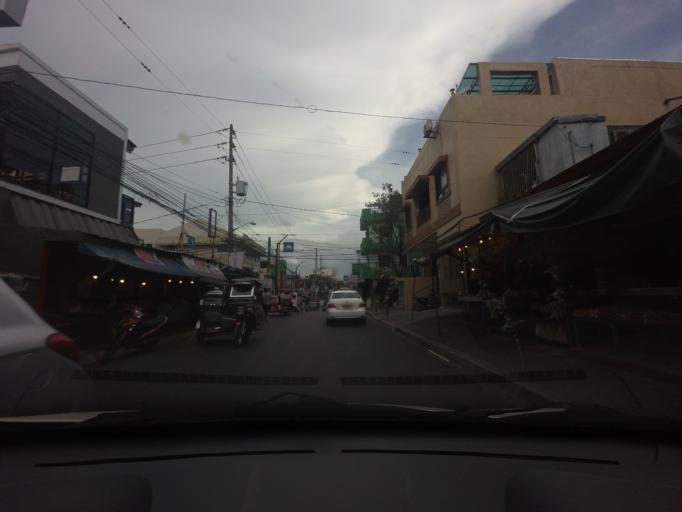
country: PH
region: Calabarzon
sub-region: Province of Rizal
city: Taguig
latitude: 14.5071
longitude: 121.0537
